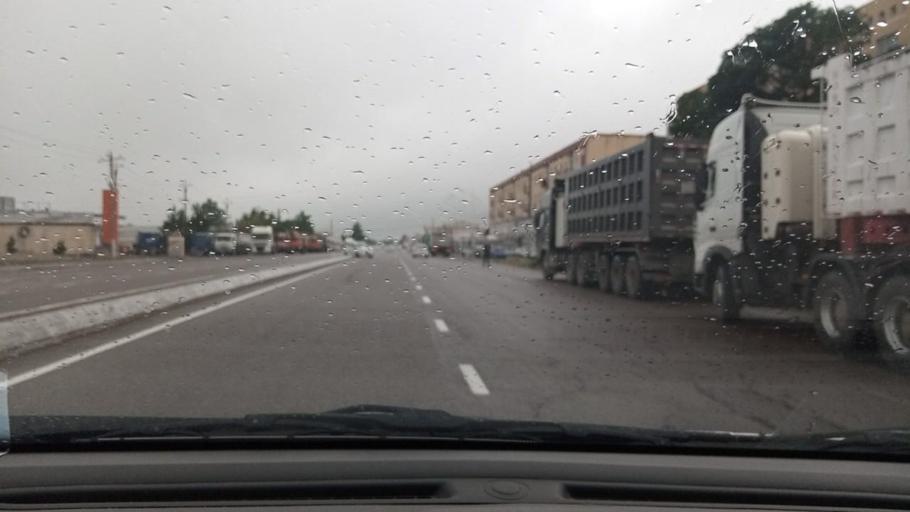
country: UZ
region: Toshkent
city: Angren
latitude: 41.0106
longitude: 70.0986
